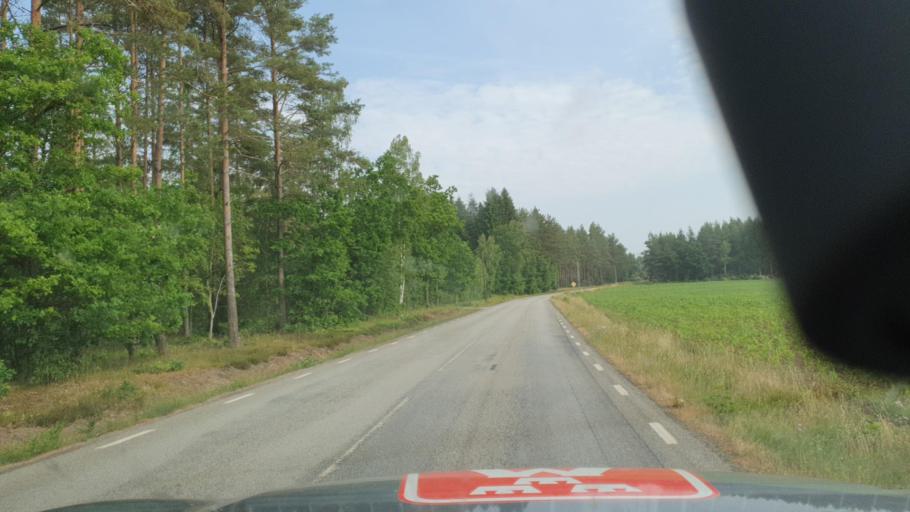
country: SE
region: Kalmar
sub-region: Kalmar Kommun
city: Trekanten
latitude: 56.6323
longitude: 16.0314
